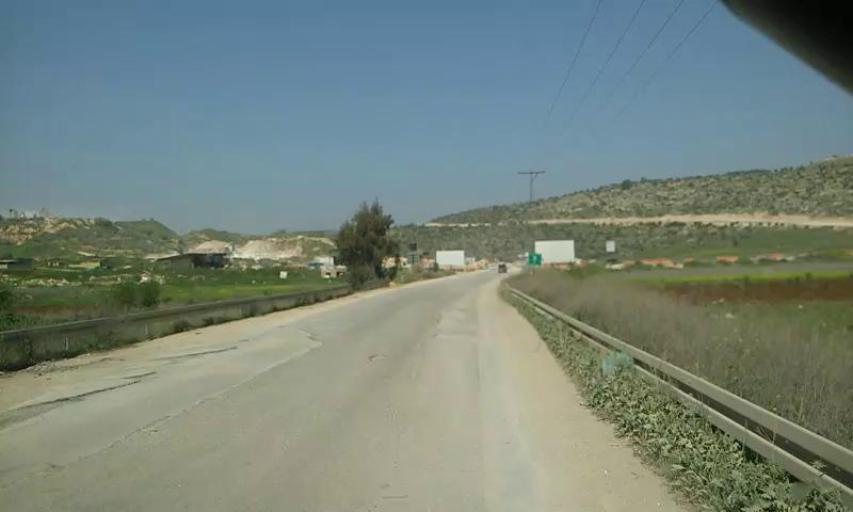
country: PS
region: West Bank
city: Az Zababidah
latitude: 32.3992
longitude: 35.3185
